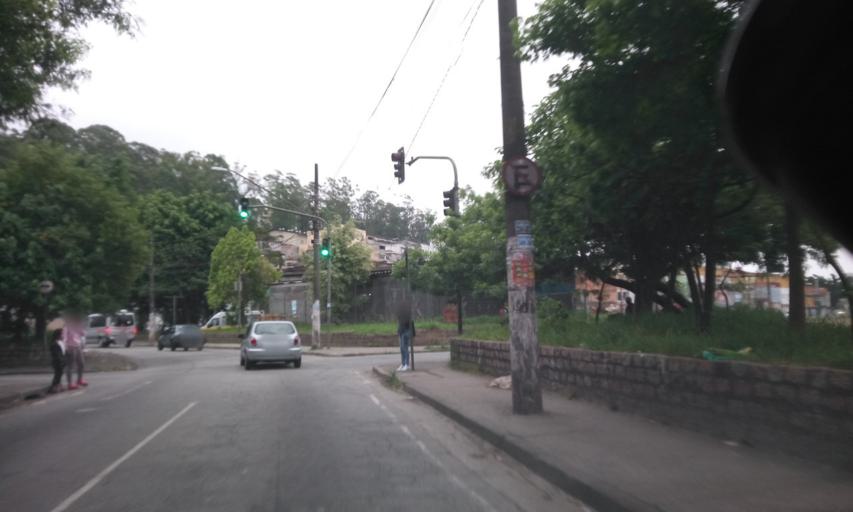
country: BR
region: Sao Paulo
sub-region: Sao Bernardo Do Campo
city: Sao Bernardo do Campo
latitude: -23.7096
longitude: -46.5300
